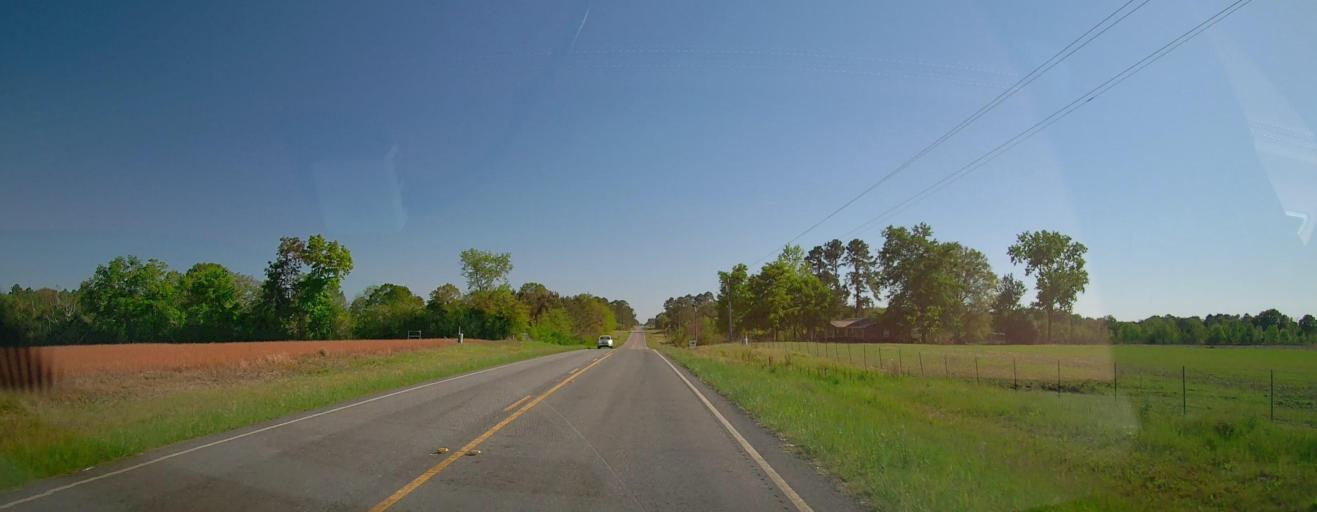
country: US
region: Georgia
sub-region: Wilcox County
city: Rochelle
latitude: 32.0697
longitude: -83.5035
